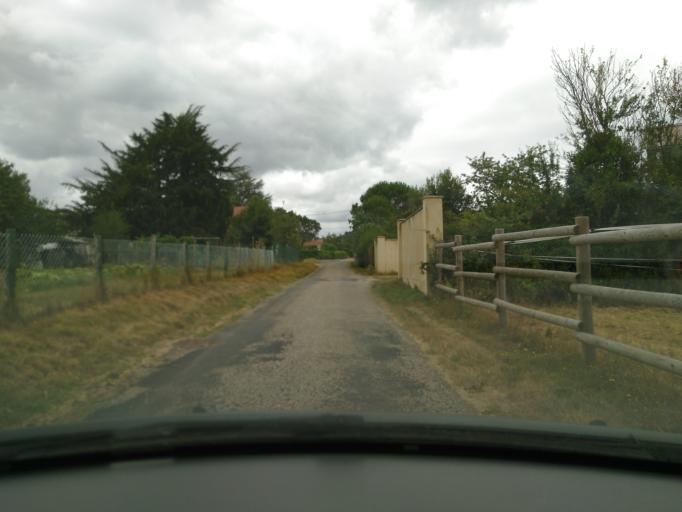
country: FR
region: Rhone-Alpes
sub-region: Departement de l'Isere
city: La Cote-Saint-Andre
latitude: 45.4280
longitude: 5.2223
